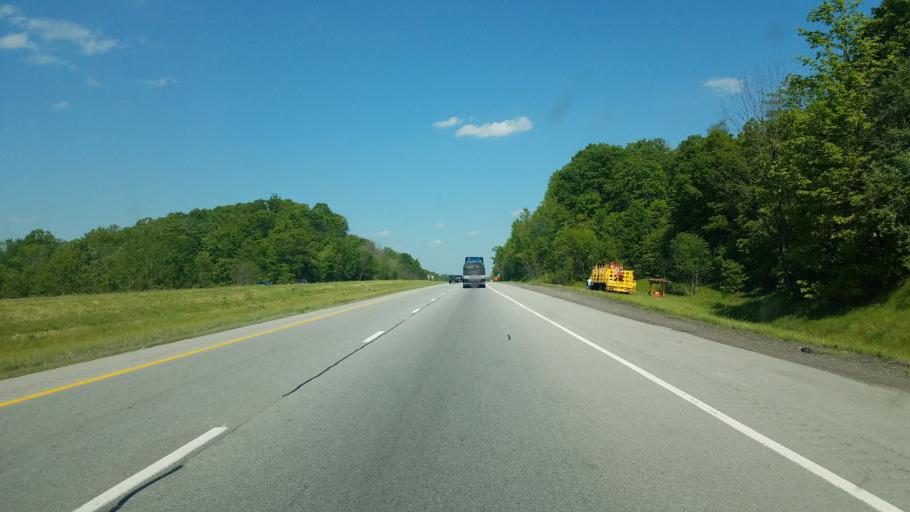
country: US
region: Ohio
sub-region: Guernsey County
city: Byesville
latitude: 40.0017
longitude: -81.5483
